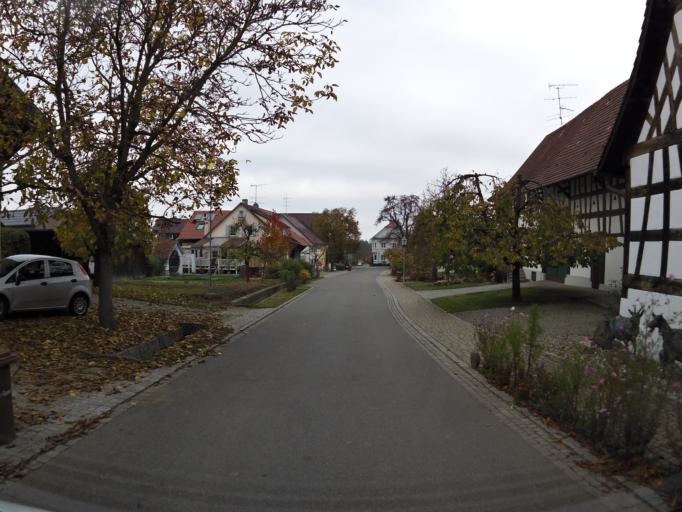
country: DE
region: Baden-Wuerttemberg
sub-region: Freiburg Region
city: Moos
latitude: 47.7094
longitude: 8.9303
